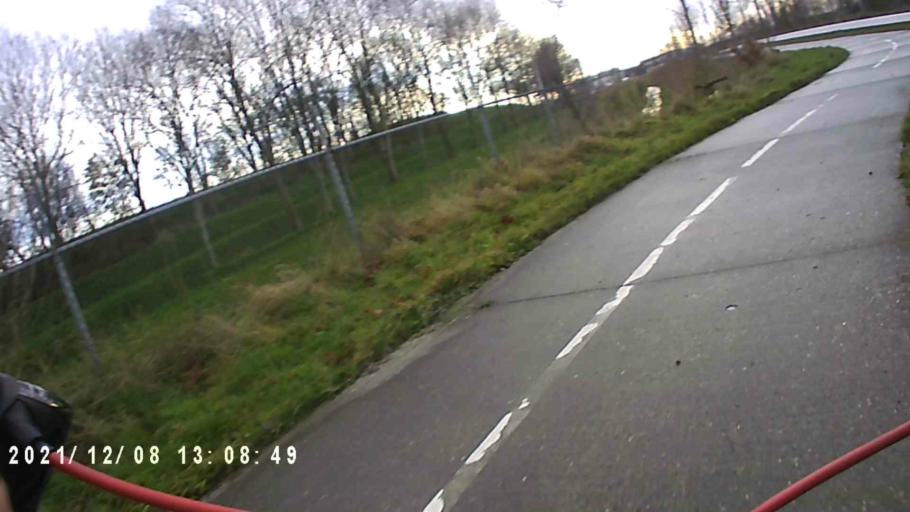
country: NL
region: Groningen
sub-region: Gemeente Haren
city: Haren
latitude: 53.2007
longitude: 6.6171
